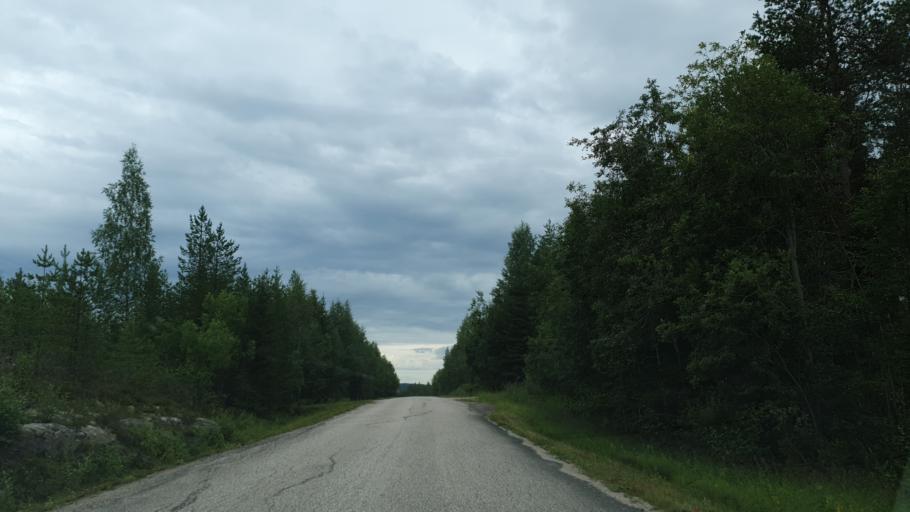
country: FI
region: Kainuu
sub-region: Kehys-Kainuu
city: Kuhmo
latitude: 64.3469
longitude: 29.2610
